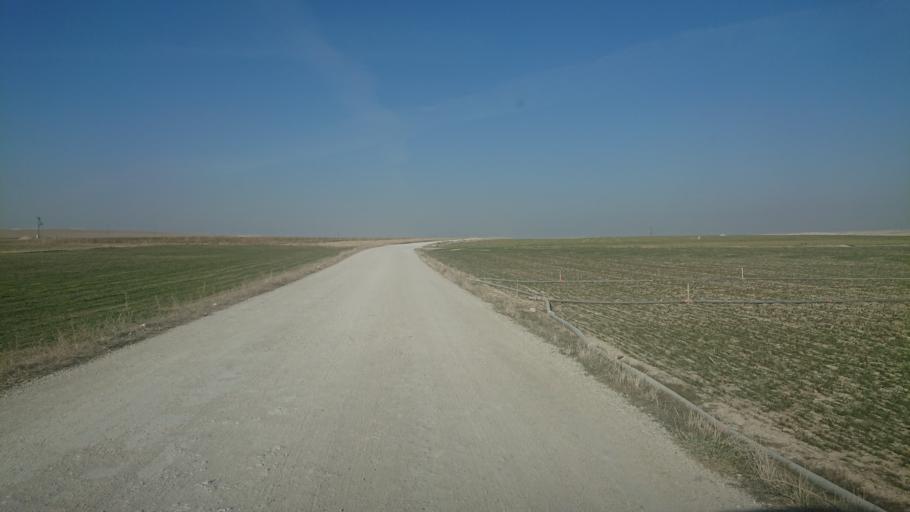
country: TR
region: Aksaray
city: Sultanhani
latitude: 38.0408
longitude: 33.6058
